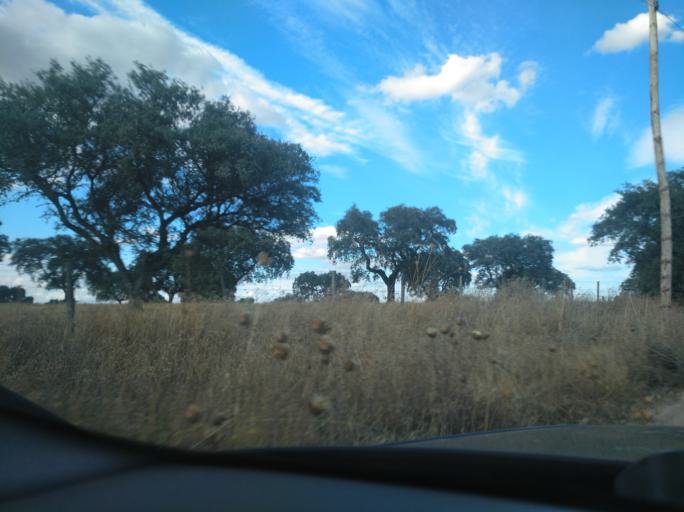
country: PT
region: Portalegre
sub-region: Campo Maior
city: Campo Maior
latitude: 39.0700
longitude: -7.1102
